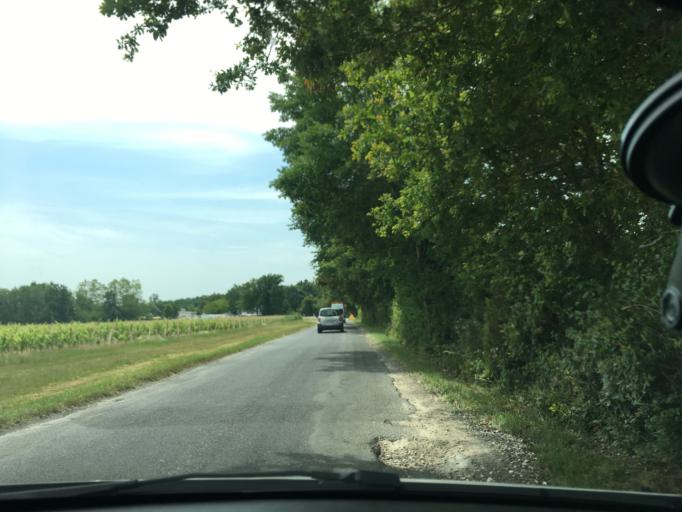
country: FR
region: Aquitaine
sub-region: Departement de la Gironde
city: Castelnau-de-Medoc
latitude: 45.0393
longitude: -0.8034
